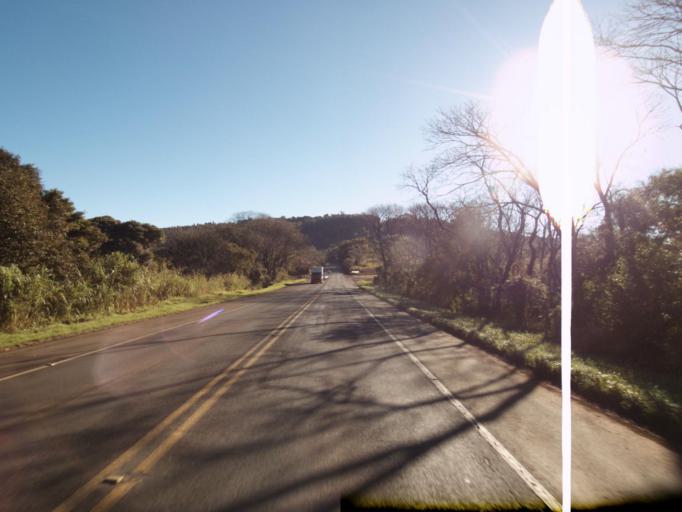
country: BR
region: Santa Catarina
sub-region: Chapeco
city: Chapeco
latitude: -26.9977
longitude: -52.6992
